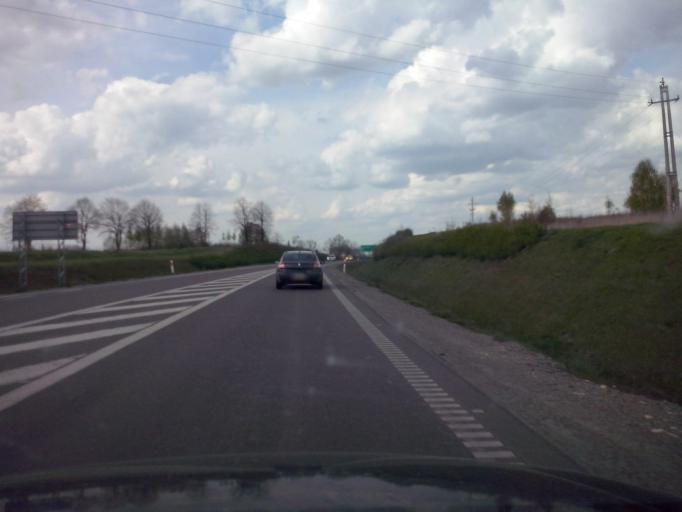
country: PL
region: Subcarpathian Voivodeship
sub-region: Powiat rzeszowski
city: Wolka Podlesna
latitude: 50.1509
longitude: 22.0775
